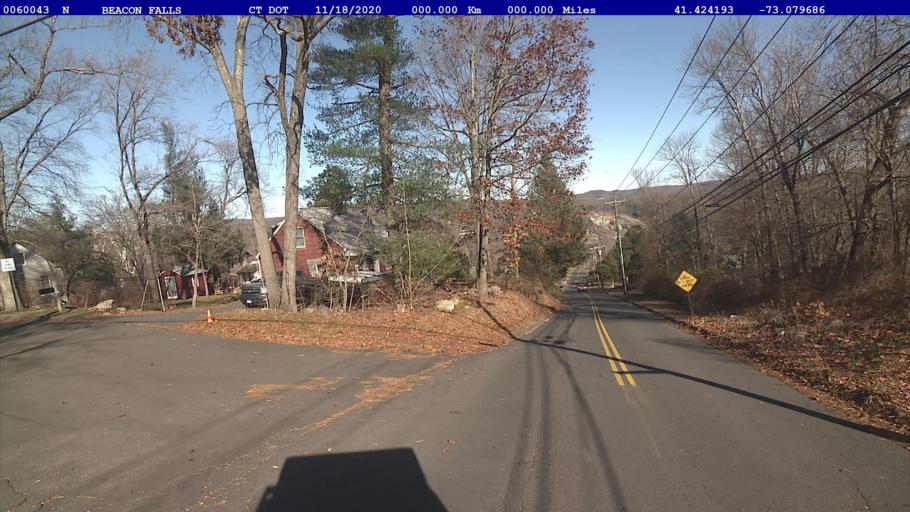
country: US
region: Connecticut
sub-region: New Haven County
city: Seymour
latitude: 41.4242
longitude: -73.0797
